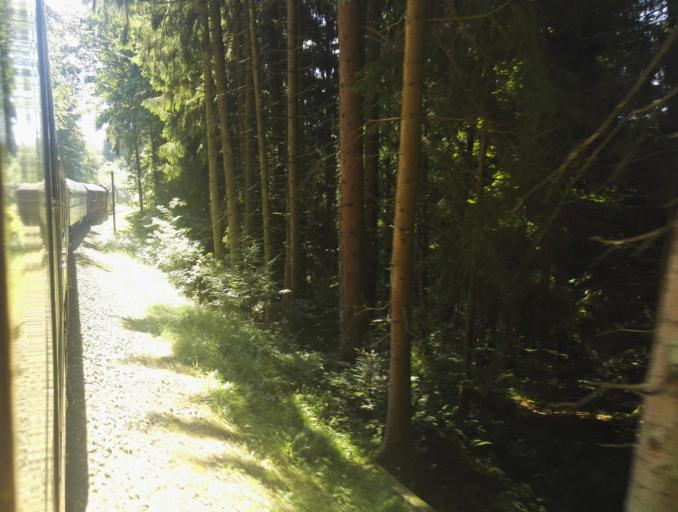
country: DE
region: Baden-Wuerttemberg
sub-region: Regierungsbezirk Stuttgart
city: Welzheim
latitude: 48.8678
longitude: 9.6188
